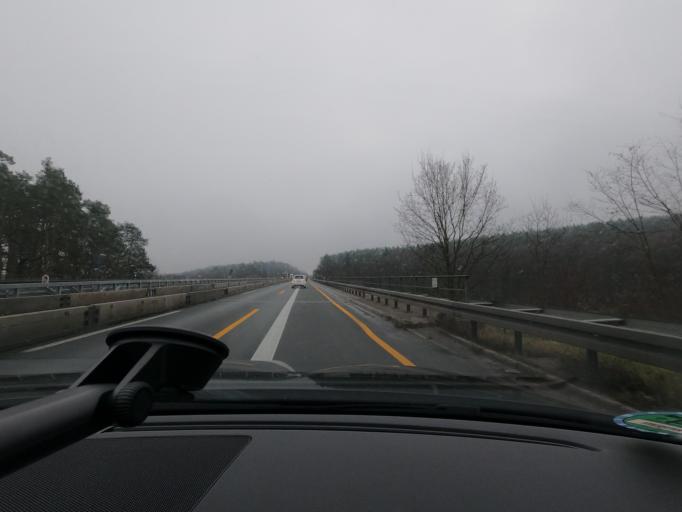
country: DE
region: Bavaria
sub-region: Upper Franconia
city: Strullendorf
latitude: 49.8554
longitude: 10.9793
